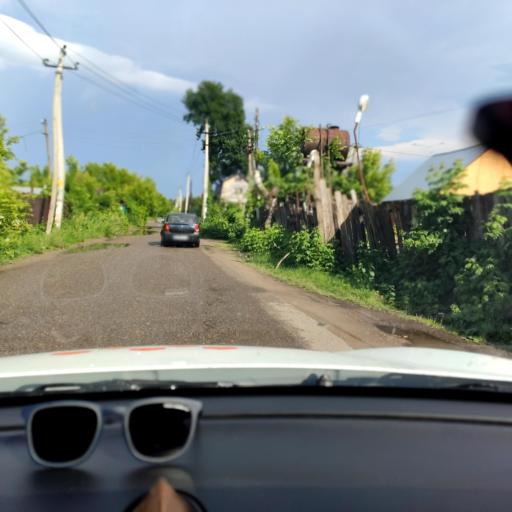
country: RU
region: Tatarstan
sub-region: Zelenodol'skiy Rayon
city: Vasil'yevo
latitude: 55.8279
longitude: 48.7546
